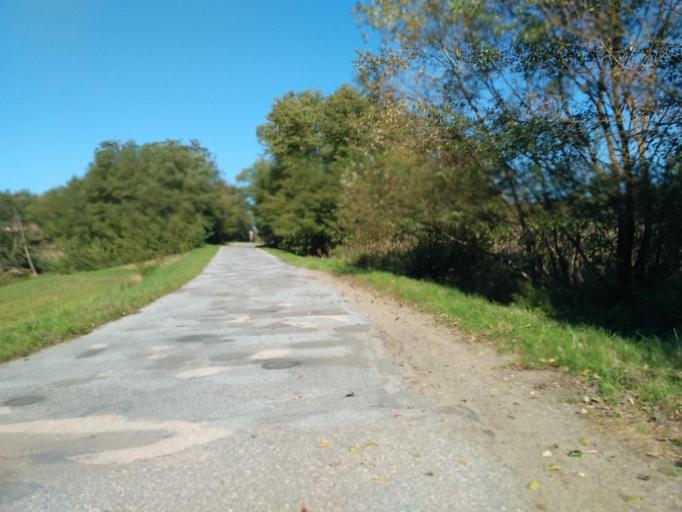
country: PL
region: Subcarpathian Voivodeship
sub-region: Powiat debicki
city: Debica
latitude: 49.9715
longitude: 21.3839
